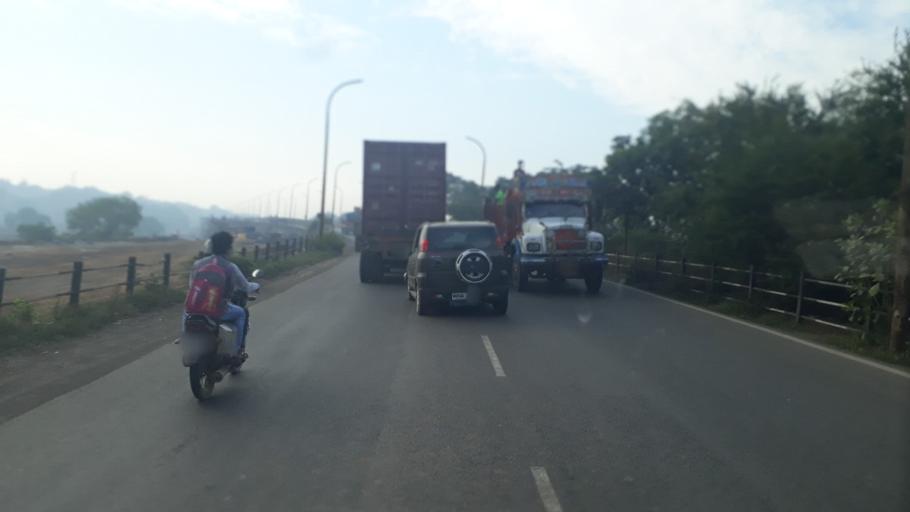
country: IN
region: Maharashtra
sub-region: Raigarh
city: Pen
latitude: 18.8421
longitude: 73.0931
